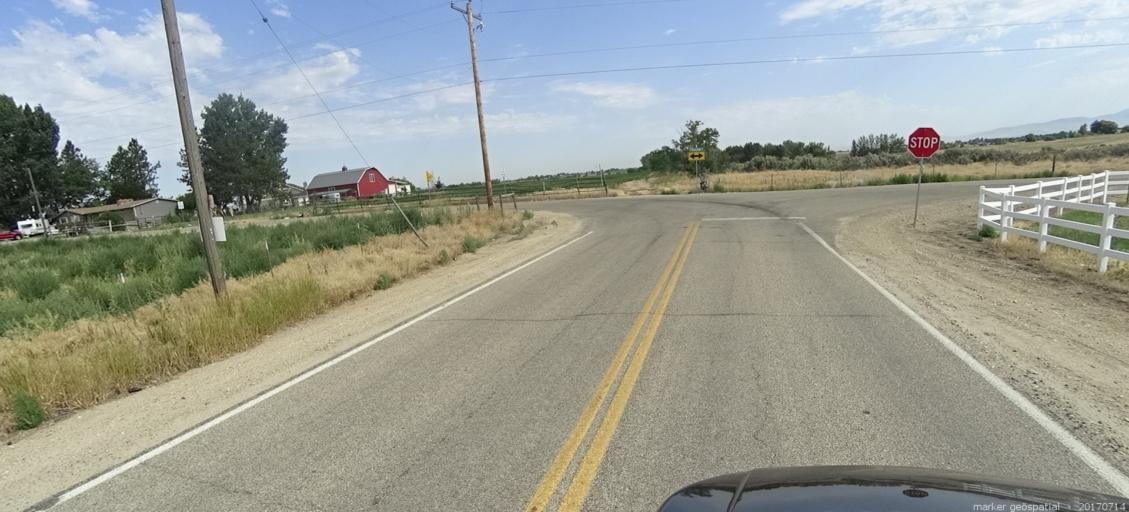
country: US
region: Idaho
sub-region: Ada County
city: Kuna
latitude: 43.5024
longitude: -116.3543
